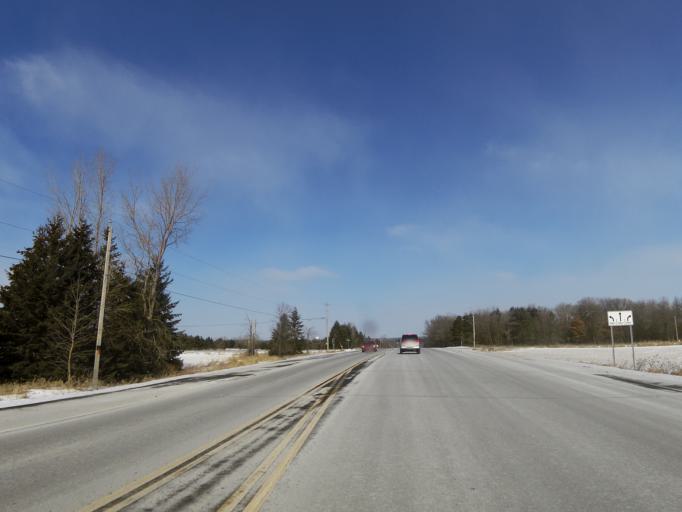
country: US
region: Minnesota
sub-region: Washington County
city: Oakdale
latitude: 44.9695
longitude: -92.9339
